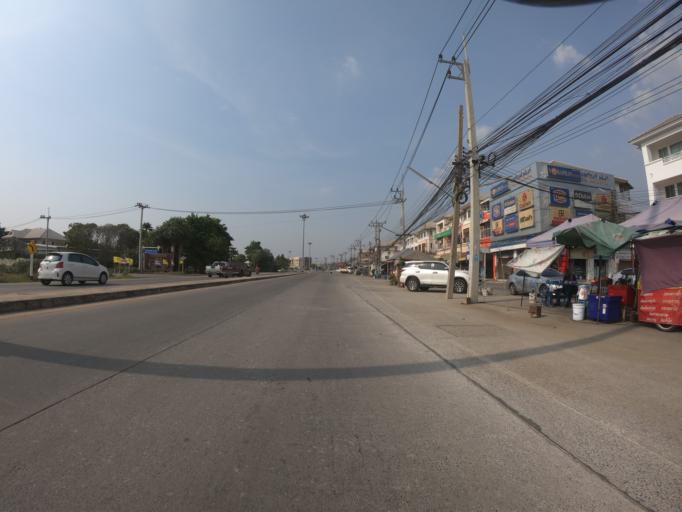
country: TH
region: Phra Nakhon Si Ayutthaya
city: Phra Nakhon Si Ayutthaya
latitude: 14.3363
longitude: 100.6048
